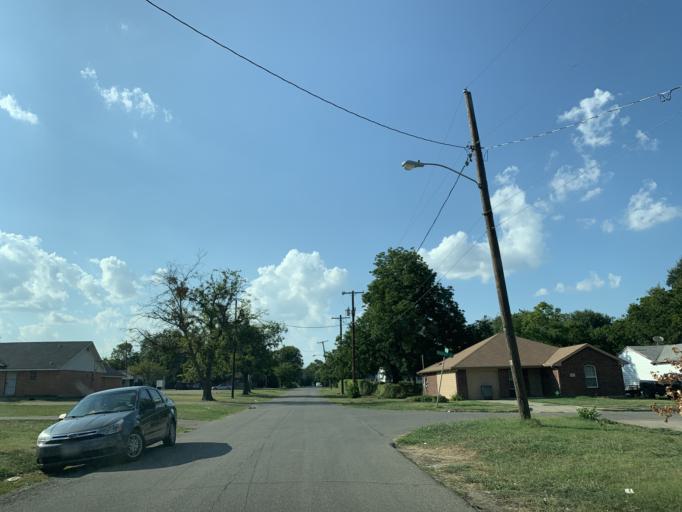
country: US
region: Texas
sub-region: Dallas County
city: Hutchins
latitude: 32.6983
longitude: -96.7782
